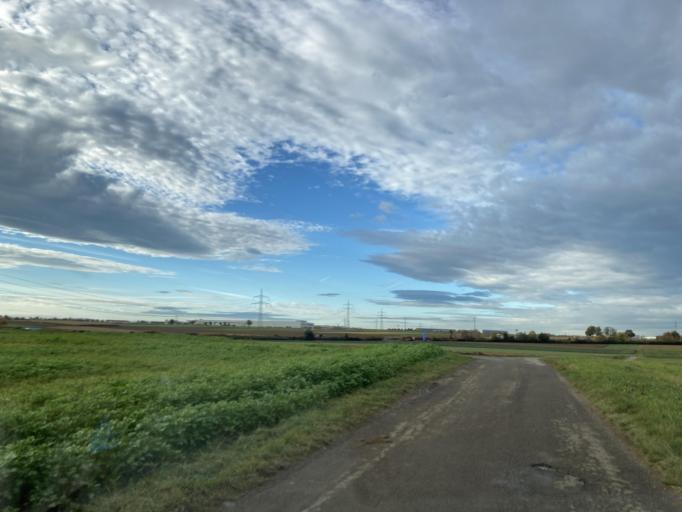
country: DE
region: Baden-Wuerttemberg
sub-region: Regierungsbezirk Stuttgart
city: Bondorf
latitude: 48.4906
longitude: 8.8369
